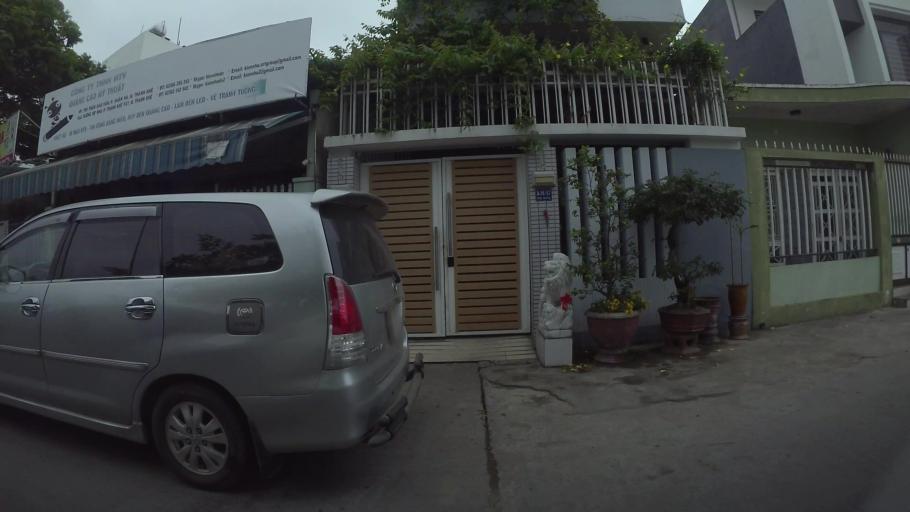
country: VN
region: Da Nang
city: Thanh Khe
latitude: 16.0669
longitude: 108.1780
